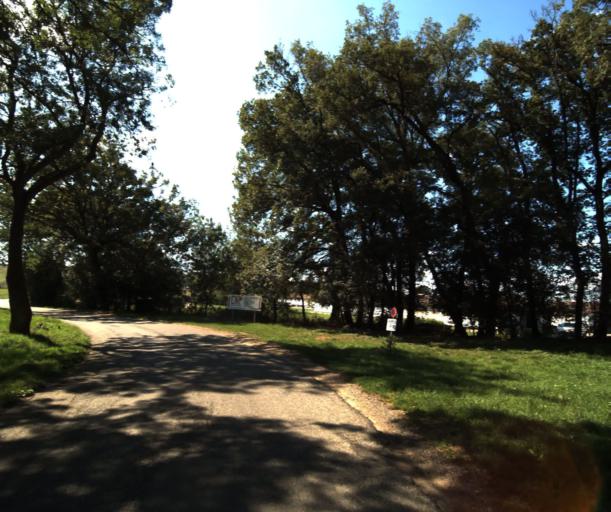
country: FR
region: Midi-Pyrenees
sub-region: Departement de la Haute-Garonne
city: Fonsorbes
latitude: 43.4978
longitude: 1.2267
